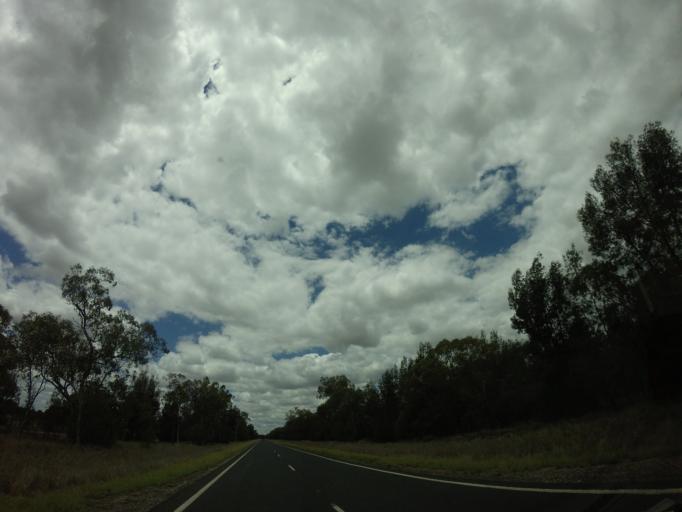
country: AU
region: Queensland
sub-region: Goondiwindi
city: Goondiwindi
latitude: -28.1623
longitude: 150.6213
